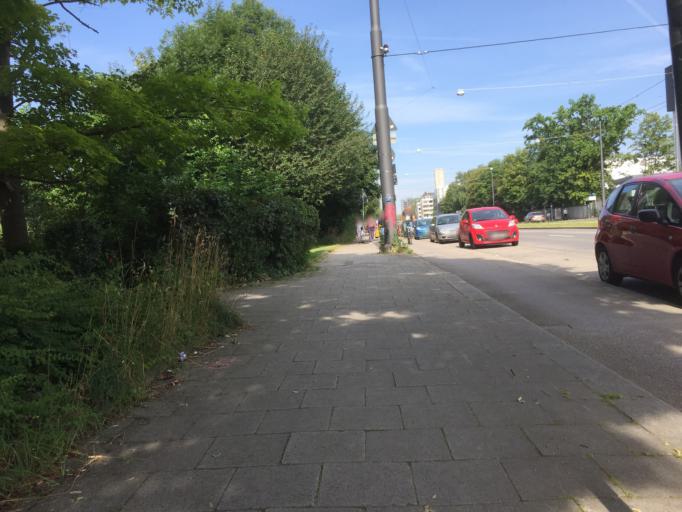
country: DE
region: Bavaria
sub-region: Upper Bavaria
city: Bogenhausen
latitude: 48.1290
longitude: 11.6266
